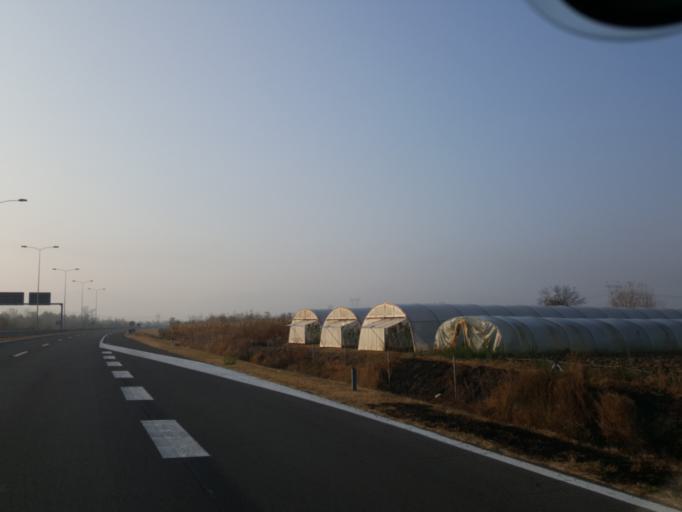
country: RS
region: Central Serbia
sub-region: Jablanicki Okrug
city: Vlasotince
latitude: 42.9671
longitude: 22.0380
